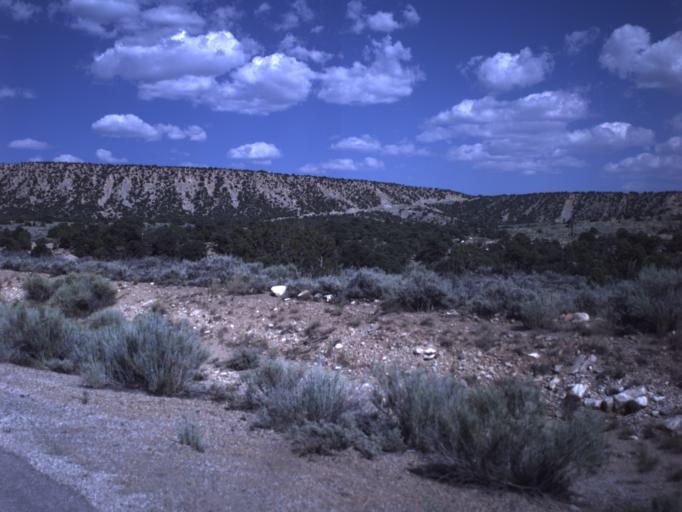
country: US
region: Utah
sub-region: Carbon County
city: Helper
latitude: 39.6735
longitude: -110.8256
